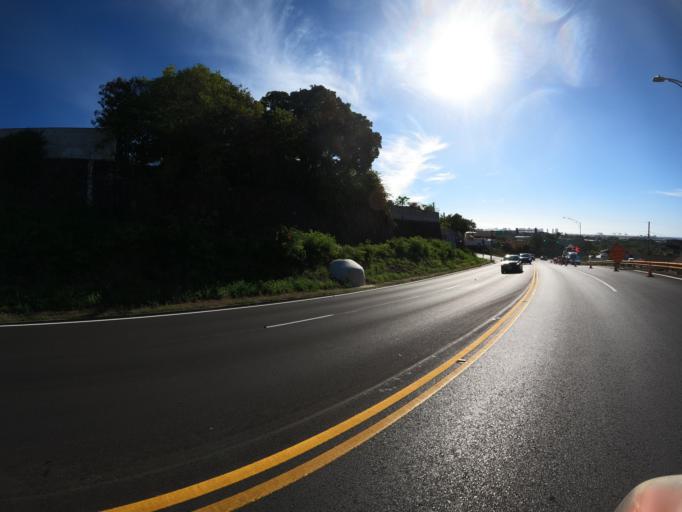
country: US
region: Hawaii
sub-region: Honolulu County
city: Halawa Heights
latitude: 21.3547
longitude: -157.8934
